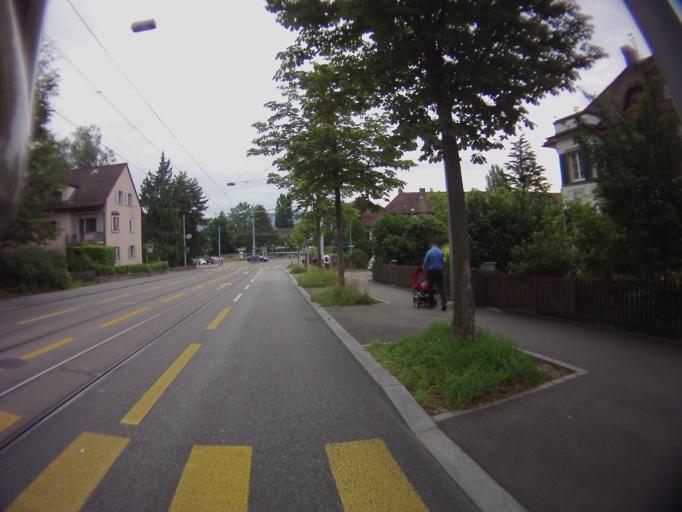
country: CH
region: Zurich
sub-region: Bezirk Zuerich
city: Zuerich (Kreis 3) / Alt-Wiedikon
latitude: 47.3582
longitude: 8.5154
